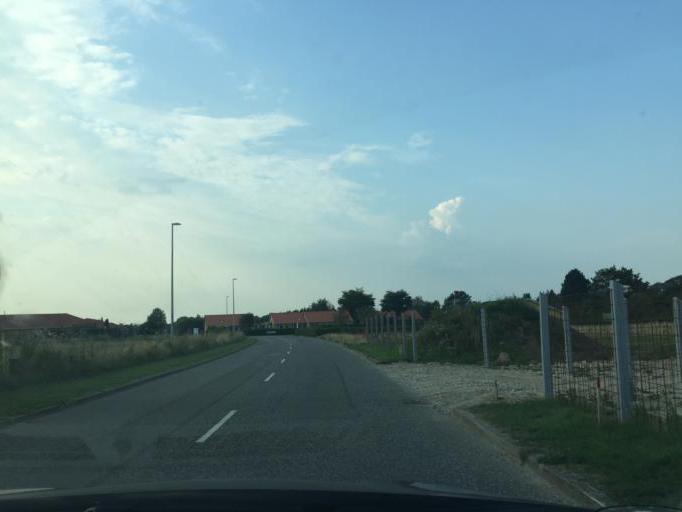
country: DK
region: South Denmark
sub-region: Kerteminde Kommune
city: Langeskov
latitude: 55.3100
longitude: 10.5945
